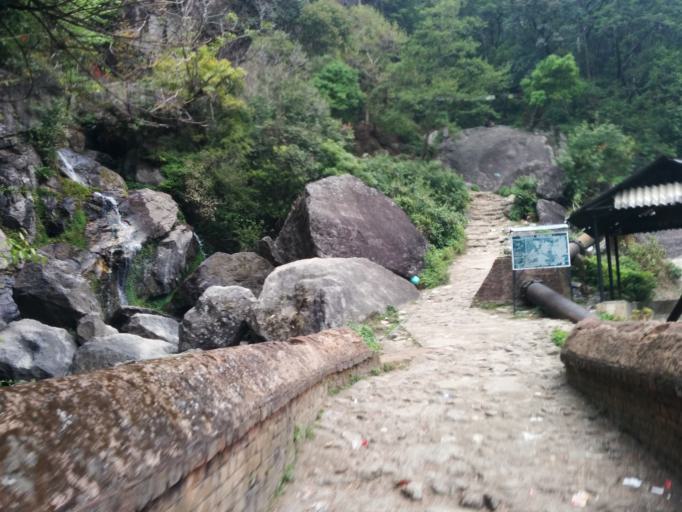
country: NP
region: Central Region
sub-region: Bagmati Zone
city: Bhaktapur
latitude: 27.7674
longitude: 85.4236
